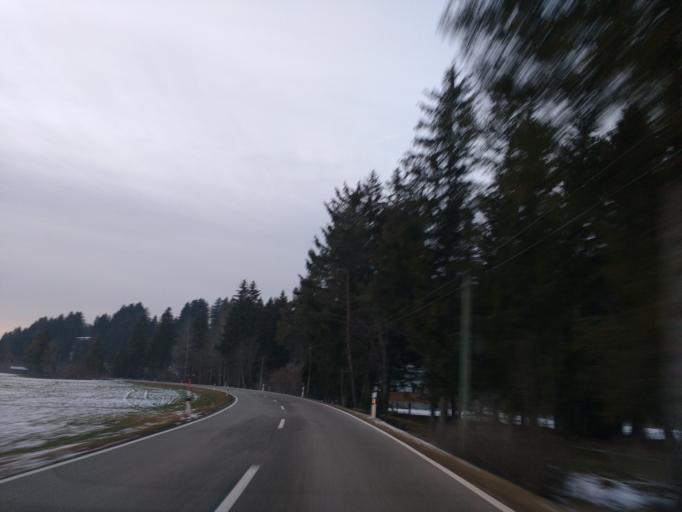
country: DE
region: Bavaria
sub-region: Swabia
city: Halblech
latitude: 47.6468
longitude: 10.8137
